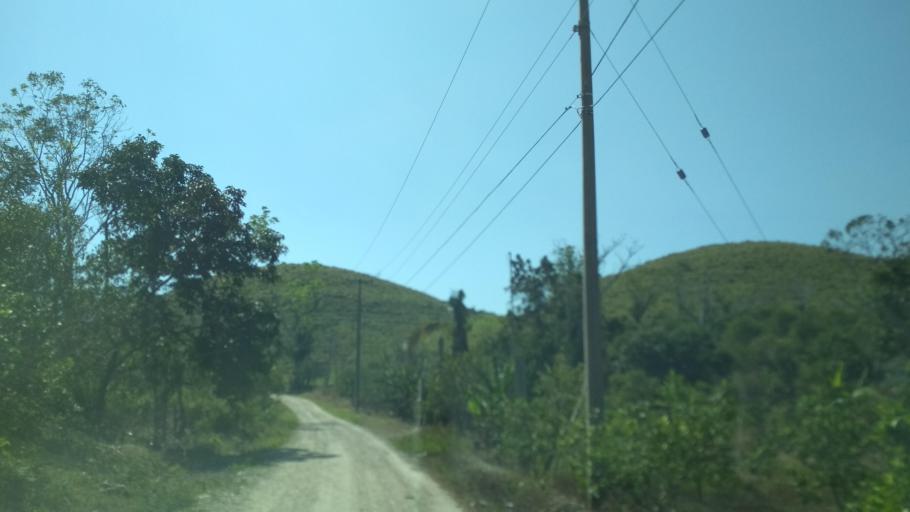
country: MX
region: Veracruz
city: Gutierrez Zamora
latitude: 20.4911
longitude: -97.1662
